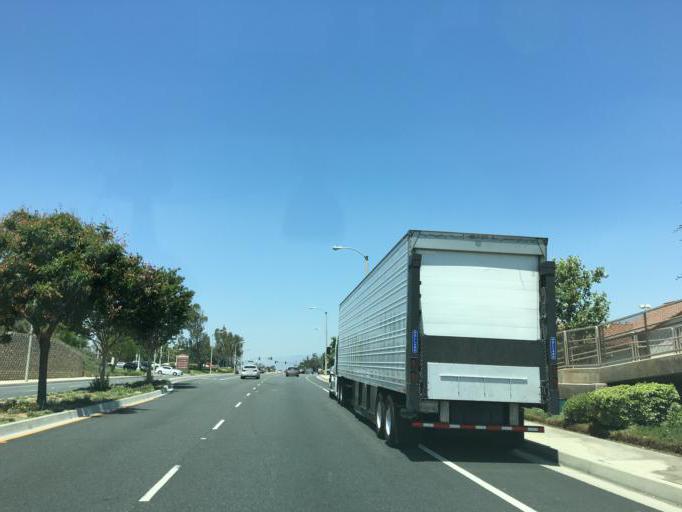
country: US
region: California
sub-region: Los Angeles County
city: Santa Clarita
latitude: 34.3910
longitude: -118.5736
